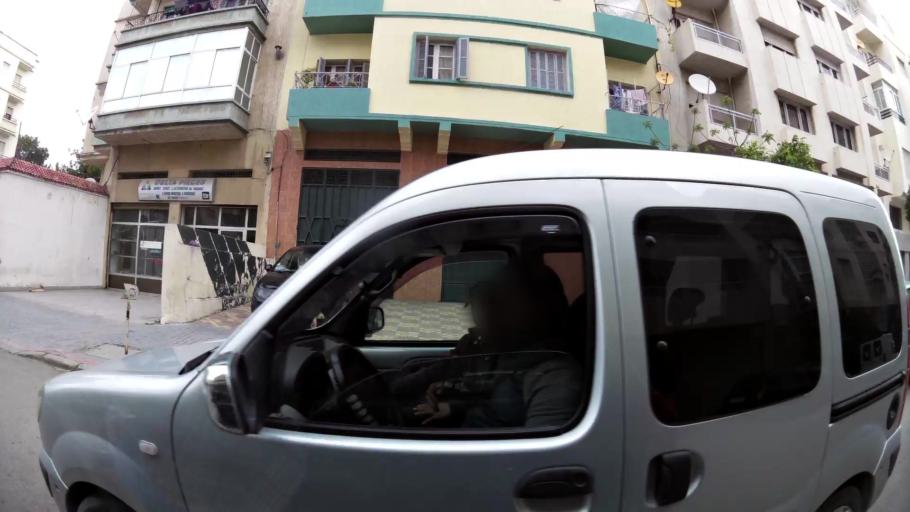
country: MA
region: Tanger-Tetouan
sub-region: Tanger-Assilah
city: Tangier
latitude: 35.7705
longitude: -5.8158
